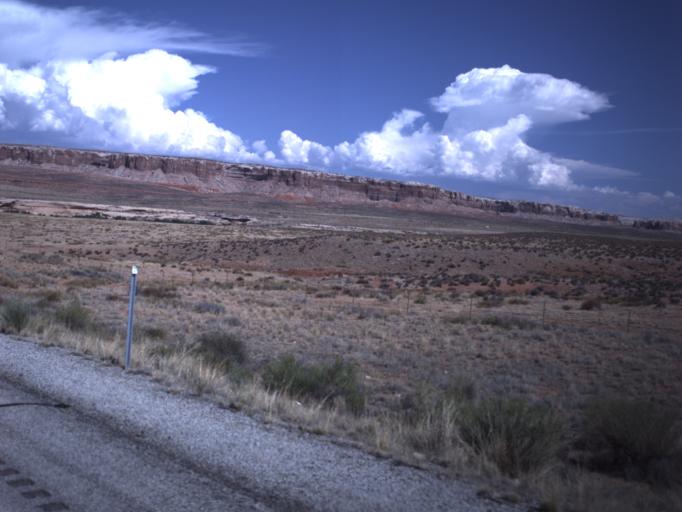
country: US
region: Utah
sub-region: San Juan County
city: Blanding
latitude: 37.2519
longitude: -109.6127
